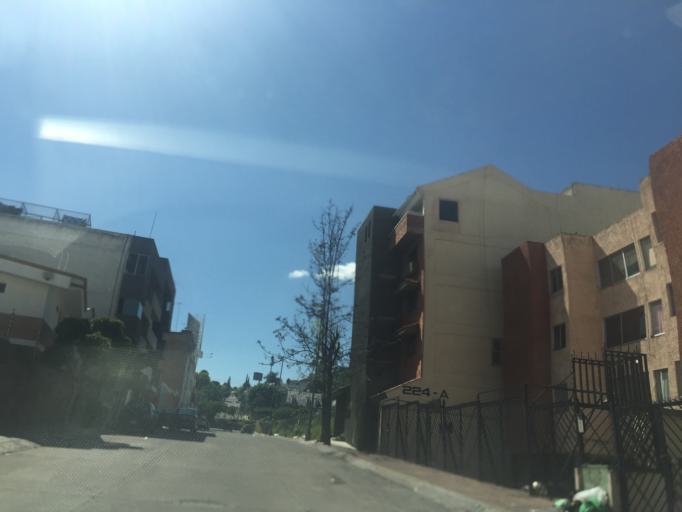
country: MX
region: Guanajuato
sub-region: Leon
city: La Ermita
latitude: 21.1540
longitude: -101.7008
